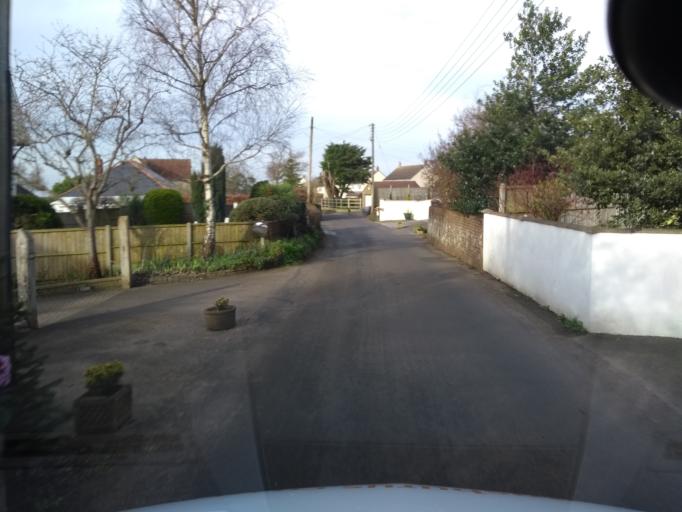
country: GB
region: England
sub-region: North Somerset
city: Bleadon
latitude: 51.3163
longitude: -2.9588
